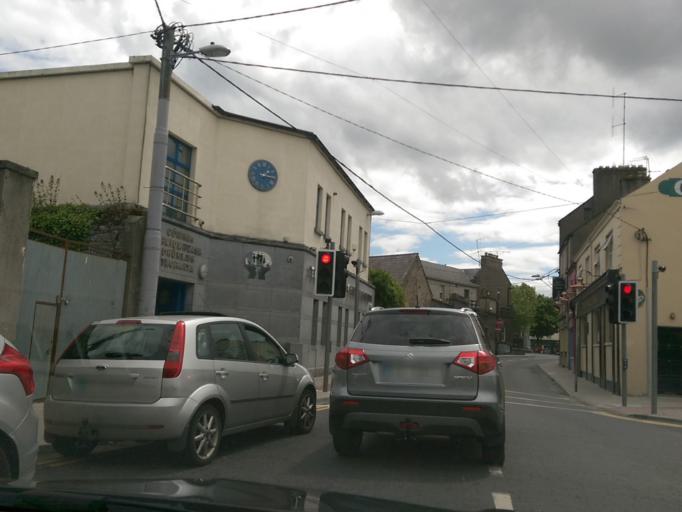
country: IE
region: Munster
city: Thurles
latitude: 52.6798
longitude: -7.8152
